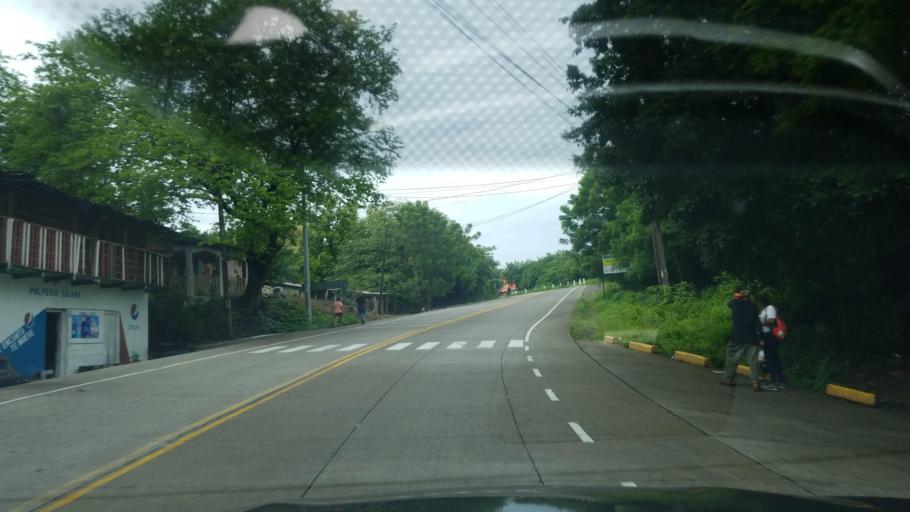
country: HN
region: Choluteca
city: Pespire
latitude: 13.6537
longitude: -87.3655
